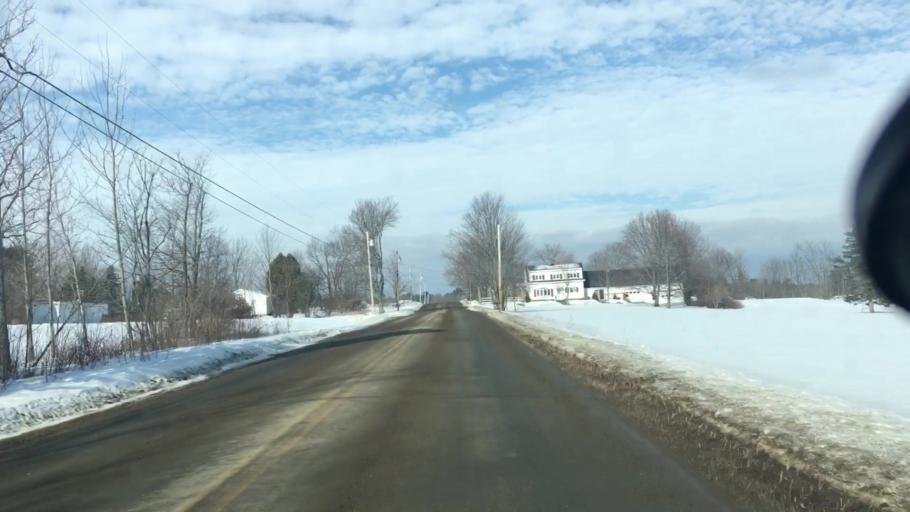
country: US
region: Maine
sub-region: Penobscot County
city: Hermon
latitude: 44.8562
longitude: -68.8780
